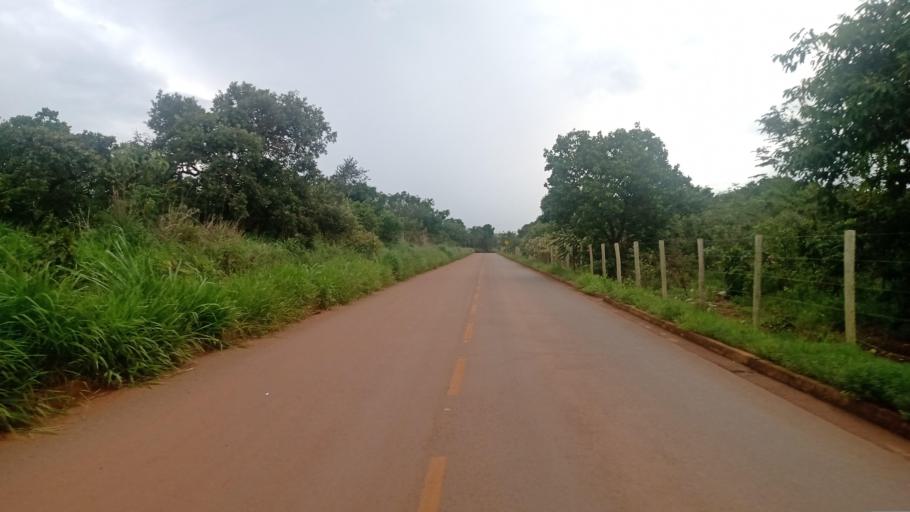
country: BR
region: Goias
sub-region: Senador Canedo
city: Senador Canedo
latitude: -16.7116
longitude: -49.1176
